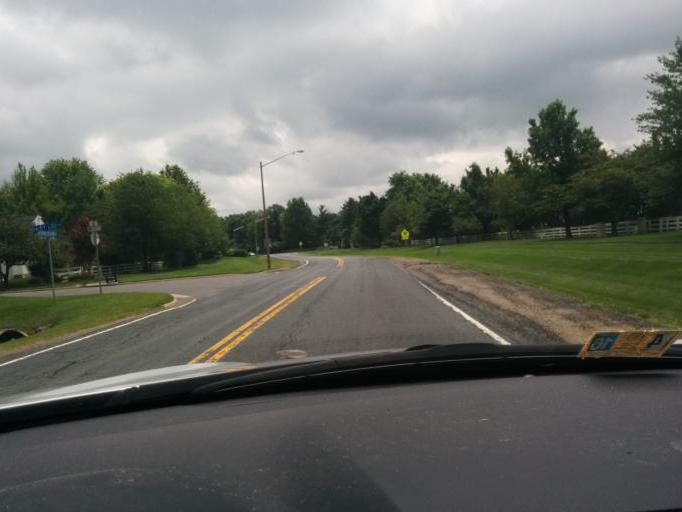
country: US
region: Virginia
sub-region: Fairfax County
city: Chantilly
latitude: 38.9124
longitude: -77.4195
